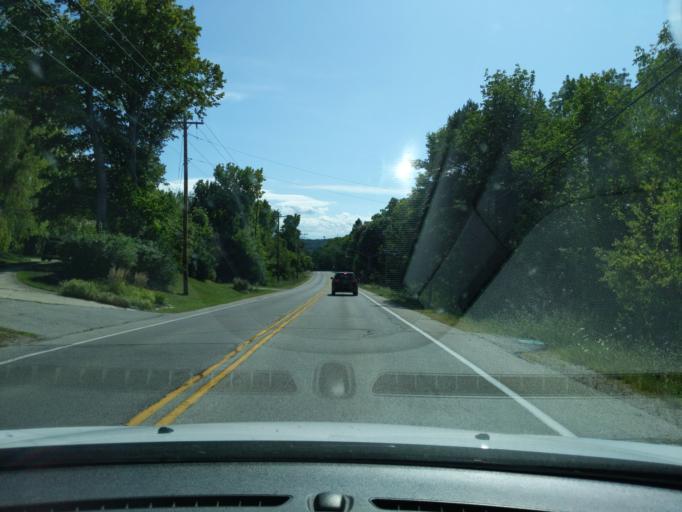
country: US
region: Wisconsin
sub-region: Door County
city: Sturgeon Bay
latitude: 45.2113
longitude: -87.1148
